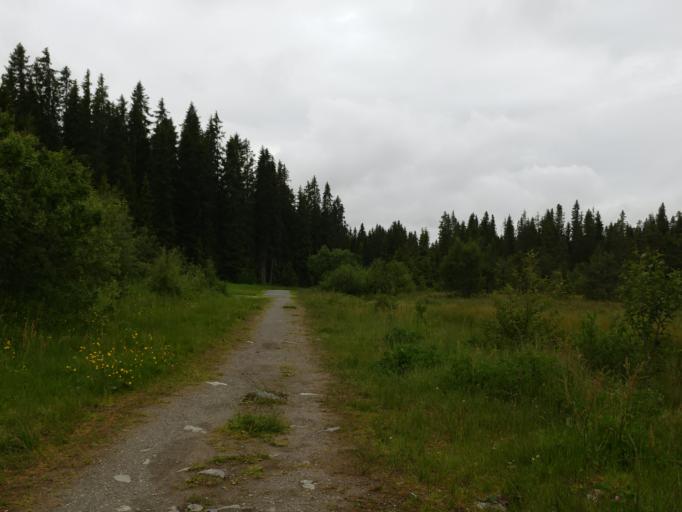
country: NO
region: Sor-Trondelag
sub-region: Trondheim
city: Trondheim
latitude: 63.3807
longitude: 10.3118
